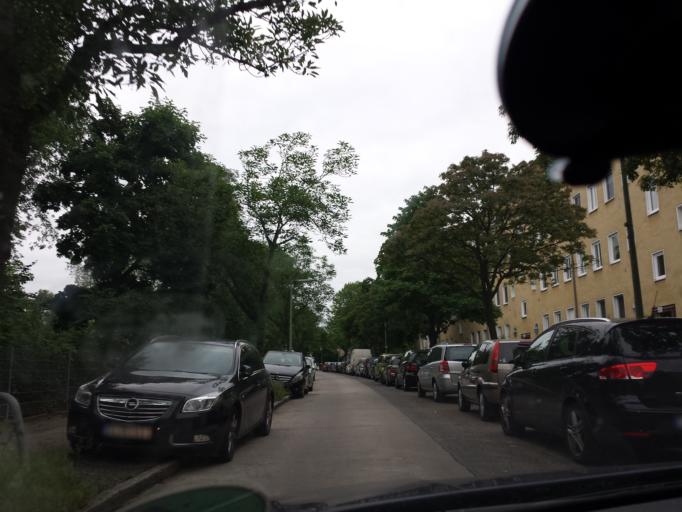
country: DE
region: Berlin
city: Westend
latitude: 52.5202
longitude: 13.2607
